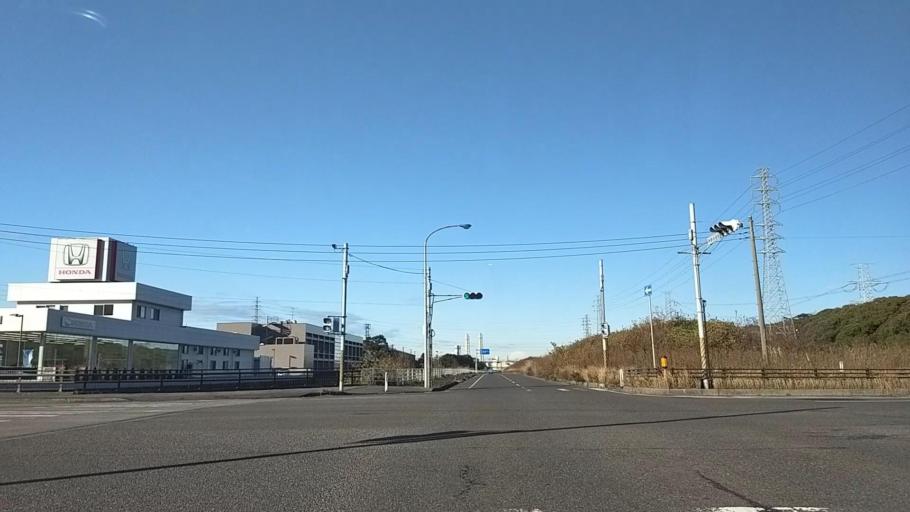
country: JP
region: Chiba
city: Kimitsu
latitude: 35.3447
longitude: 139.8759
